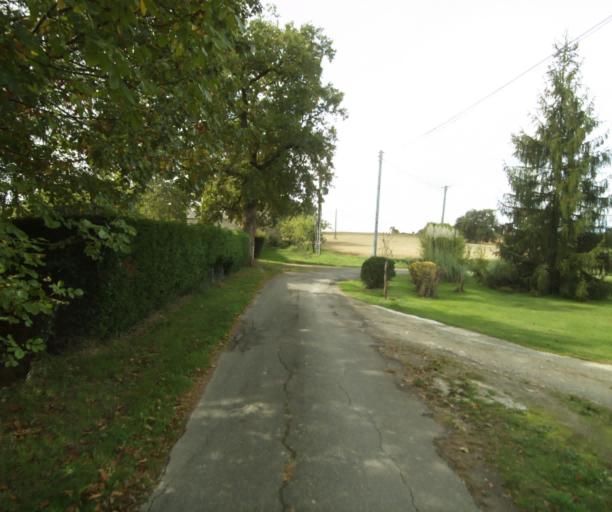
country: FR
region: Midi-Pyrenees
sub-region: Departement du Gers
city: Eauze
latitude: 43.8364
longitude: 0.0983
